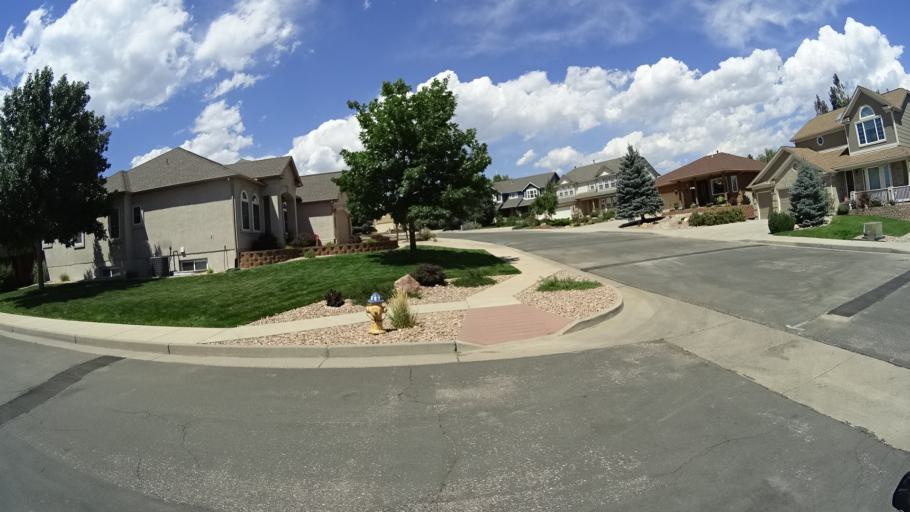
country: US
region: Colorado
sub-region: El Paso County
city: Black Forest
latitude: 38.9553
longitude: -104.7594
